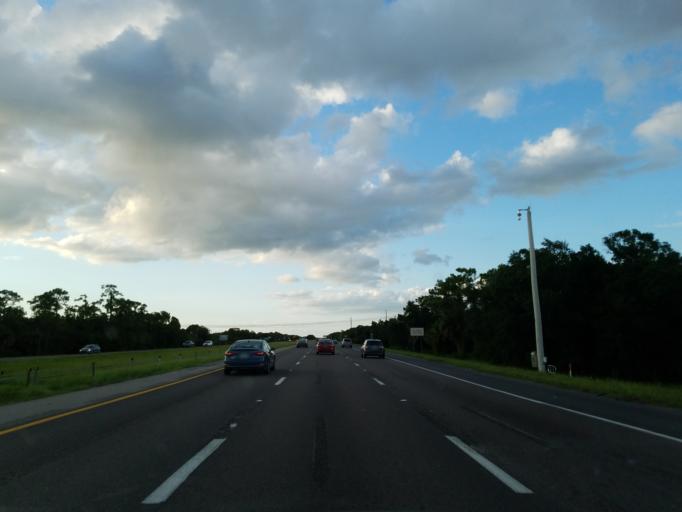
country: US
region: Florida
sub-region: Sarasota County
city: The Meadows
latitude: 27.4032
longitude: -82.4525
